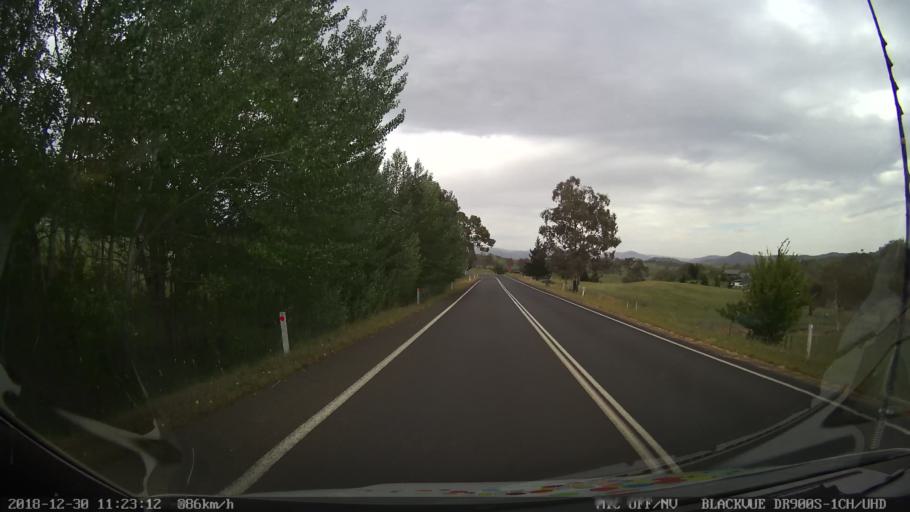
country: AU
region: New South Wales
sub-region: Snowy River
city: Jindabyne
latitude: -36.4921
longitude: 148.6655
